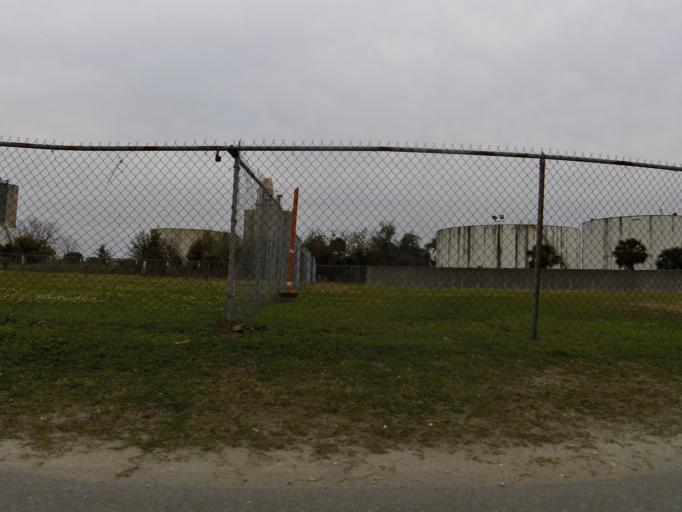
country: US
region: Florida
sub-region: Duval County
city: Jacksonville
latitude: 30.3231
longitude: -81.6311
